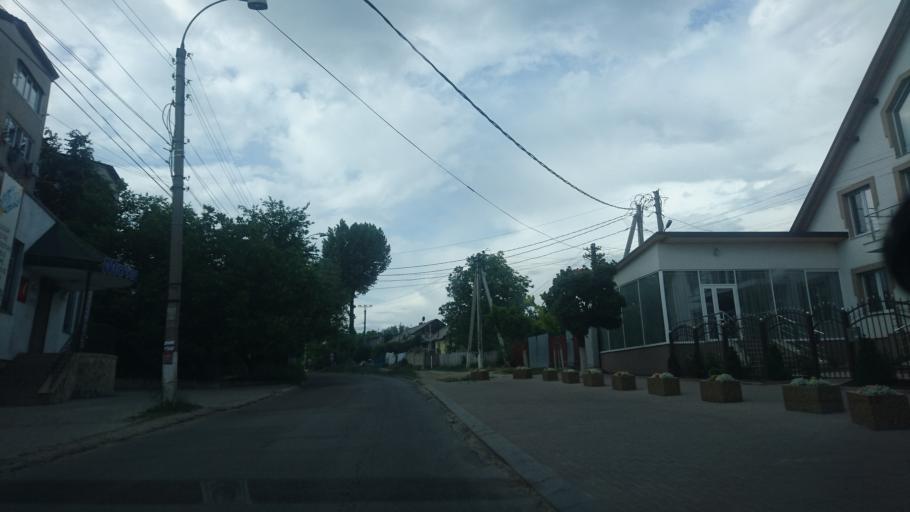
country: MD
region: Chisinau
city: Stauceni
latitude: 47.0535
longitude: 28.8420
